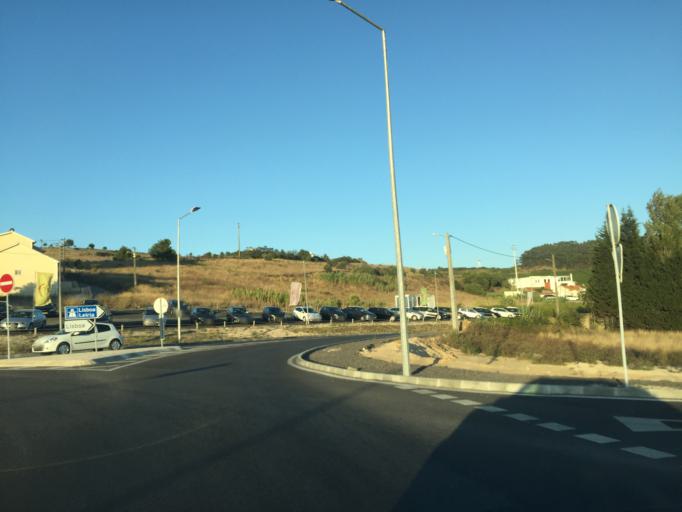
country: PT
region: Lisbon
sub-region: Torres Vedras
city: Torres Vedras
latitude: 39.0717
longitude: -9.2487
